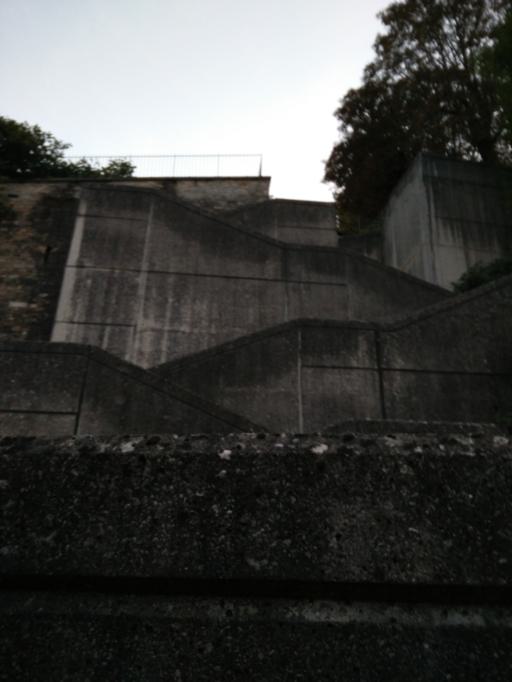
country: FR
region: Franche-Comte
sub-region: Departement de la Haute-Saone
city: Champlitte-la-Ville
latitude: 47.6167
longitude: 5.5157
